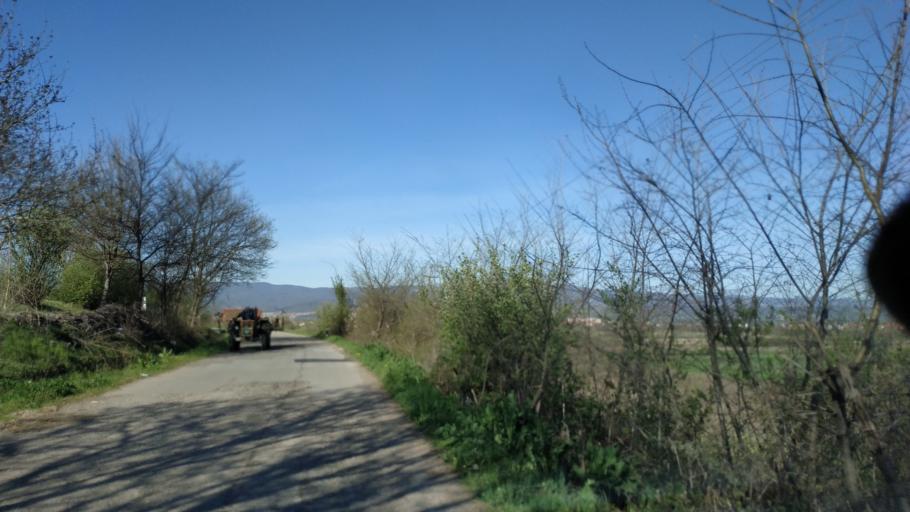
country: RS
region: Central Serbia
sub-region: Nisavski Okrug
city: Aleksinac
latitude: 43.4961
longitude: 21.6743
